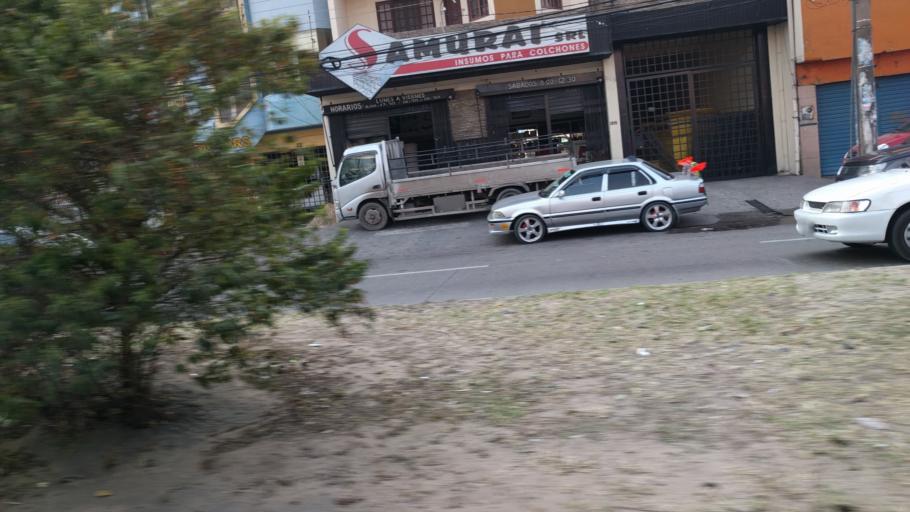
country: BO
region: Santa Cruz
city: Santa Cruz de la Sierra
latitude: -17.7840
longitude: -63.1644
